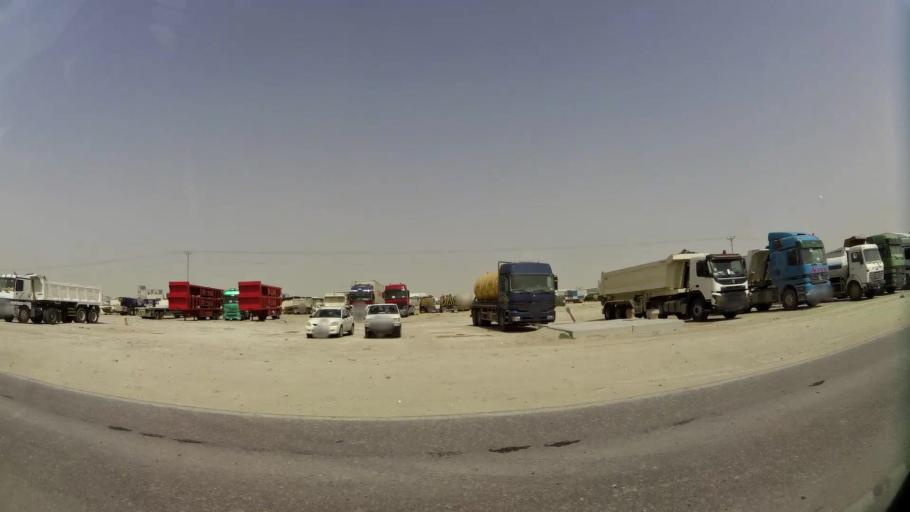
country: QA
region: Baladiyat ar Rayyan
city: Ar Rayyan
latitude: 25.2119
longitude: 51.3581
